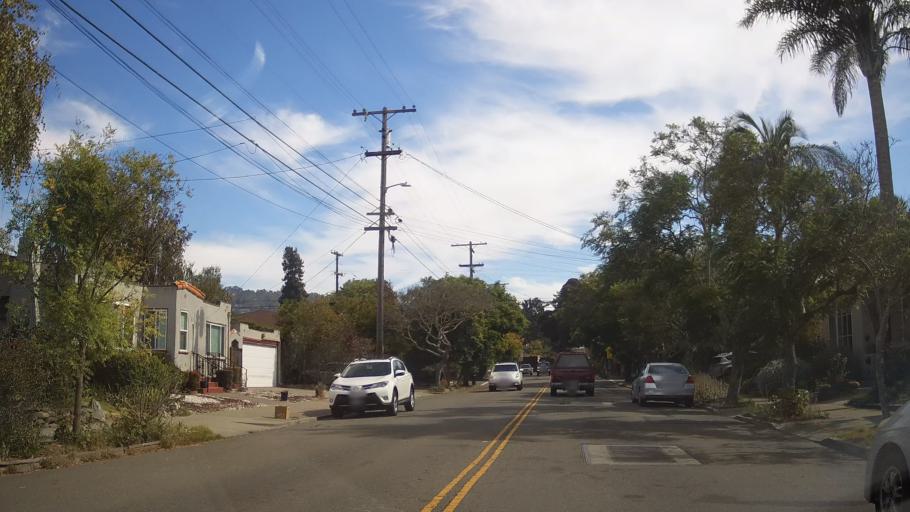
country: US
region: California
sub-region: Alameda County
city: Albany
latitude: 37.8806
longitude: -122.2864
